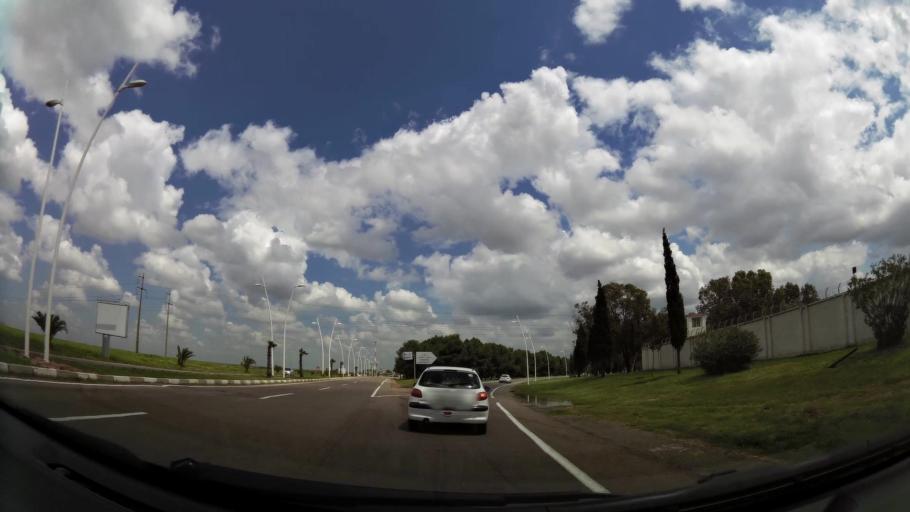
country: MA
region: Chaouia-Ouardigha
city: Nouaseur
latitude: 33.4002
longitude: -7.5735
